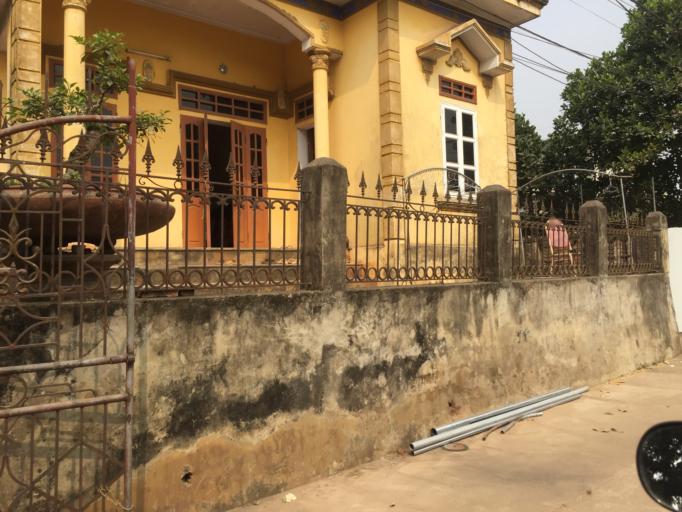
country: VN
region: Hung Yen
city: Van Giang
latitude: 20.9457
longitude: 105.9111
